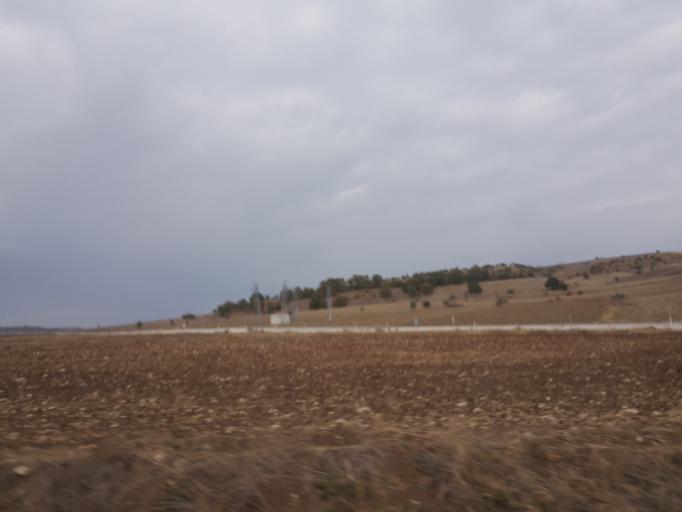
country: TR
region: Corum
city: Cemilbey
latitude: 40.2686
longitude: 35.0737
